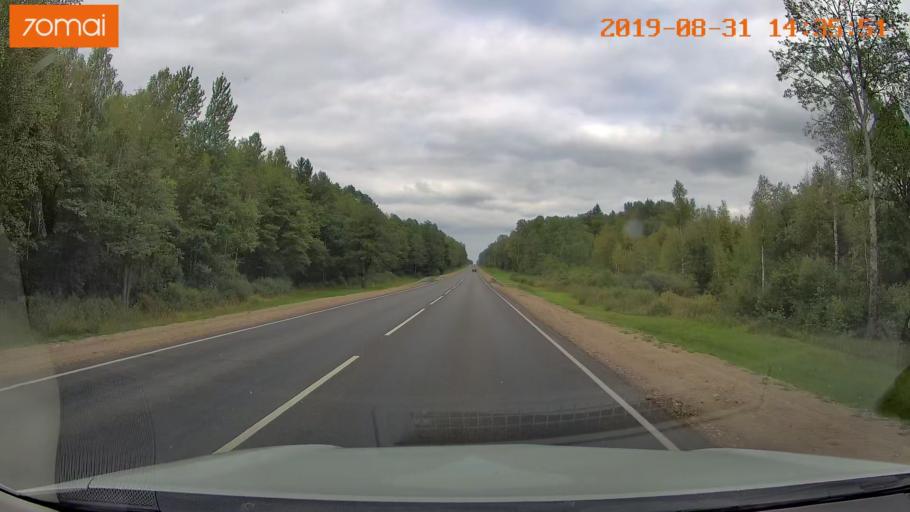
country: RU
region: Smolensk
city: Yekimovichi
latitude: 54.1657
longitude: 33.4654
